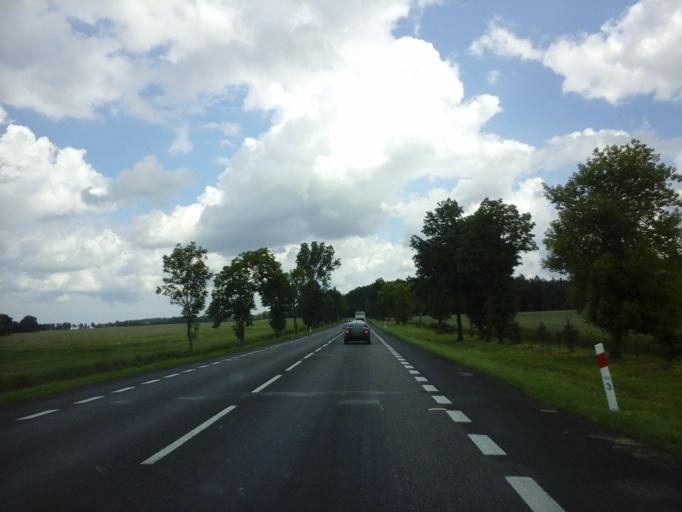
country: PL
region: West Pomeranian Voivodeship
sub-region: Powiat bialogardzki
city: Bialogard
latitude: 54.0847
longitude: 15.9840
